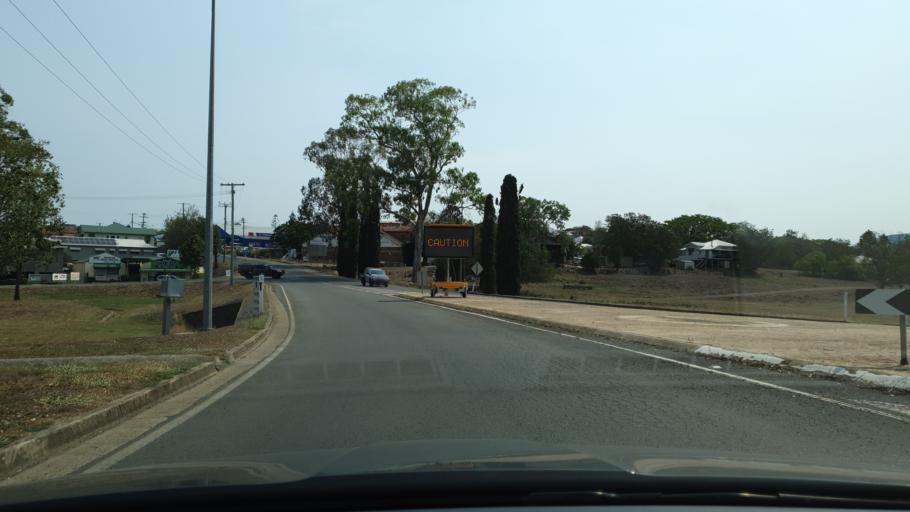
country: AU
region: Queensland
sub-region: Ipswich
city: Deebing Heights
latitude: -27.9939
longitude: 152.6827
